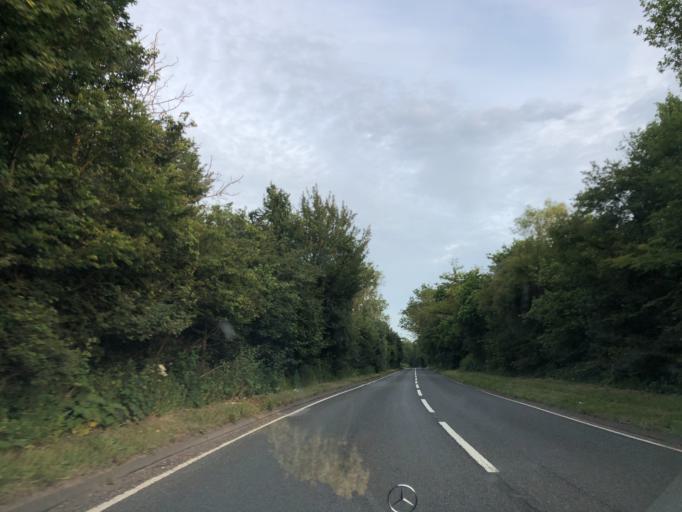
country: GB
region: England
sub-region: Solihull
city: Hampton in Arden
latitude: 52.4441
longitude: -1.6860
